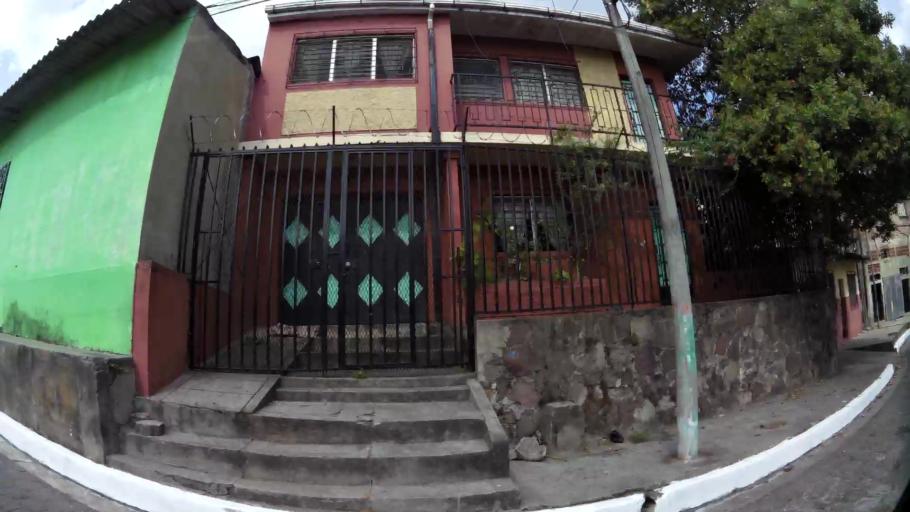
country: SV
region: San Salvador
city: Delgado
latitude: 13.7164
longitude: -89.1680
